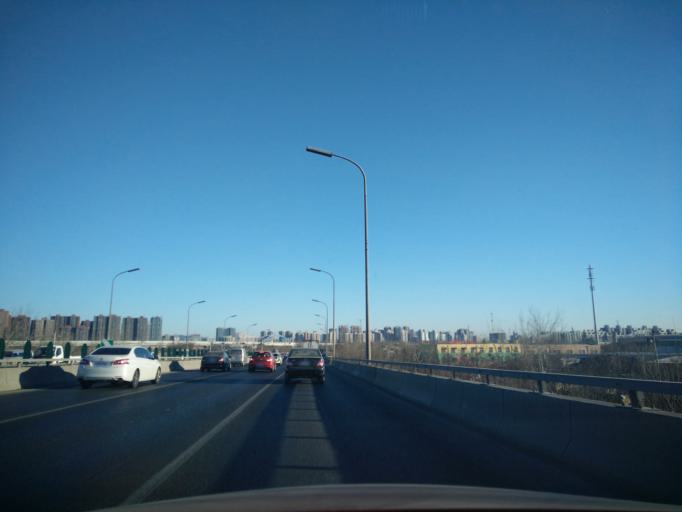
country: CN
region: Beijing
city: Lugu
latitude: 39.8819
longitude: 116.2027
